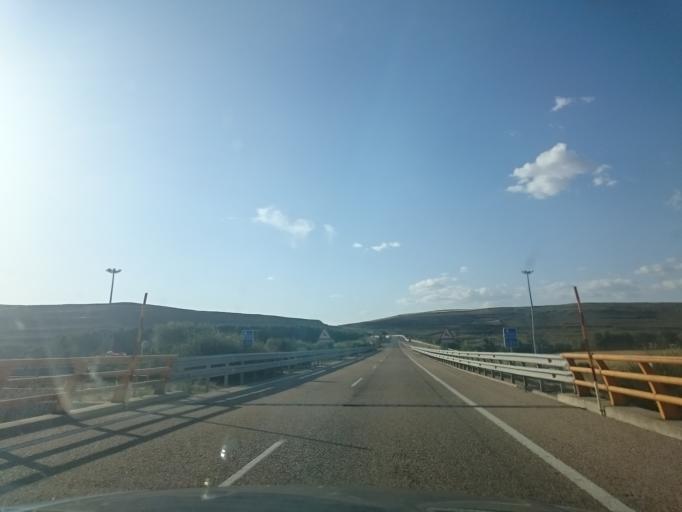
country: ES
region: Castille and Leon
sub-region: Provincia de Burgos
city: San Mames de Burgos
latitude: 42.3484
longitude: -3.7937
